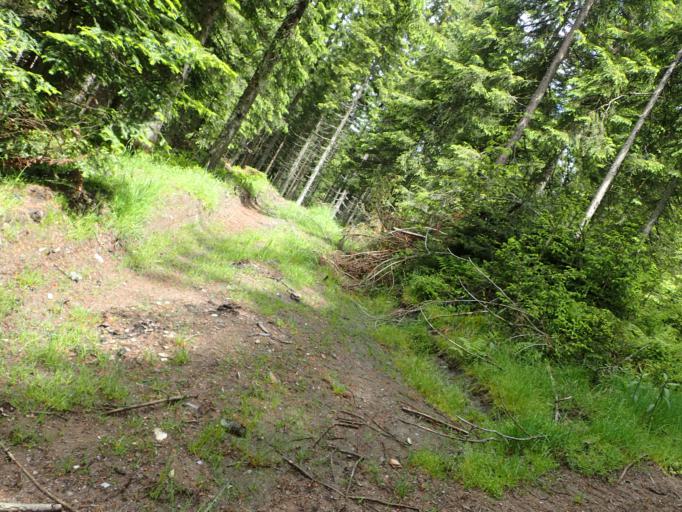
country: AT
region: Salzburg
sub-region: Politischer Bezirk Sankt Johann im Pongau
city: Wagrain
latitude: 47.3575
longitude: 13.2806
